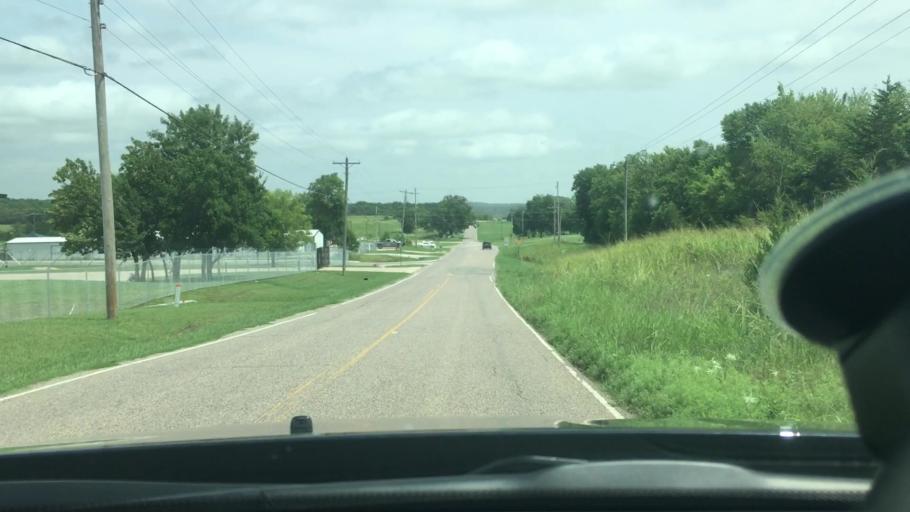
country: US
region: Oklahoma
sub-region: Pontotoc County
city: Ada
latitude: 34.7527
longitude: -96.6903
